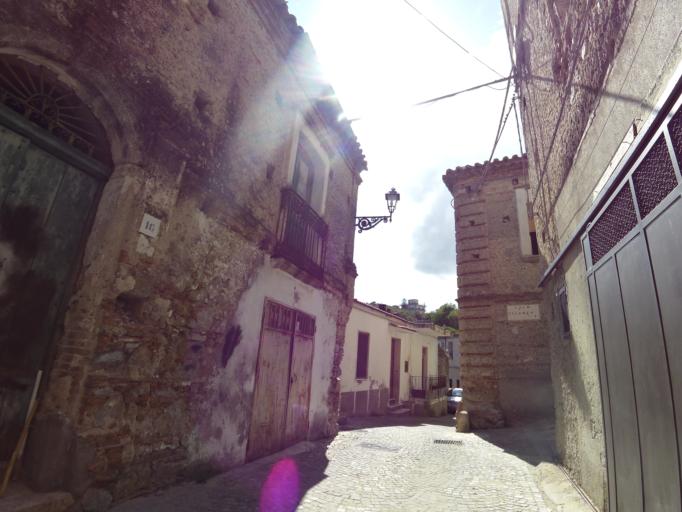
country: IT
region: Calabria
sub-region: Provincia di Reggio Calabria
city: Riace
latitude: 38.4172
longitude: 16.4838
